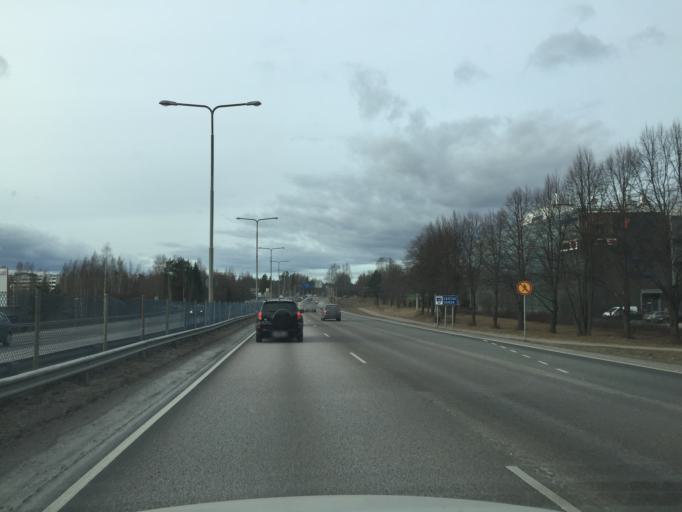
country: FI
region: Uusimaa
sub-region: Helsinki
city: Teekkarikylae
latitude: 60.2604
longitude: 24.8772
